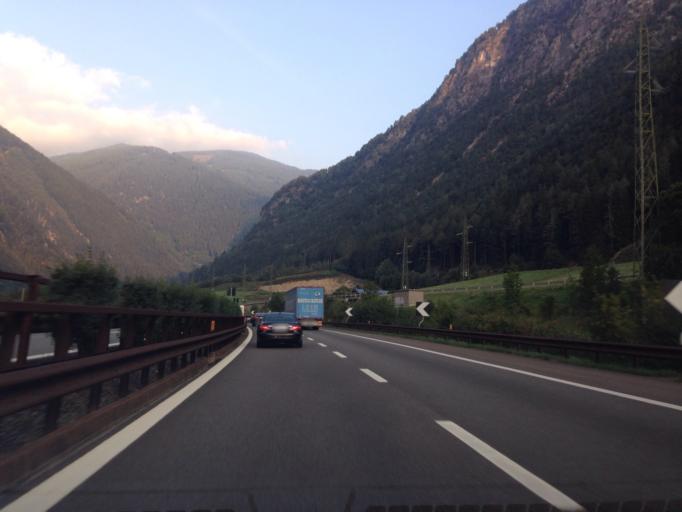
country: IT
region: Trentino-Alto Adige
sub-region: Bolzano
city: Fortezza
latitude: 46.8119
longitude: 11.5593
